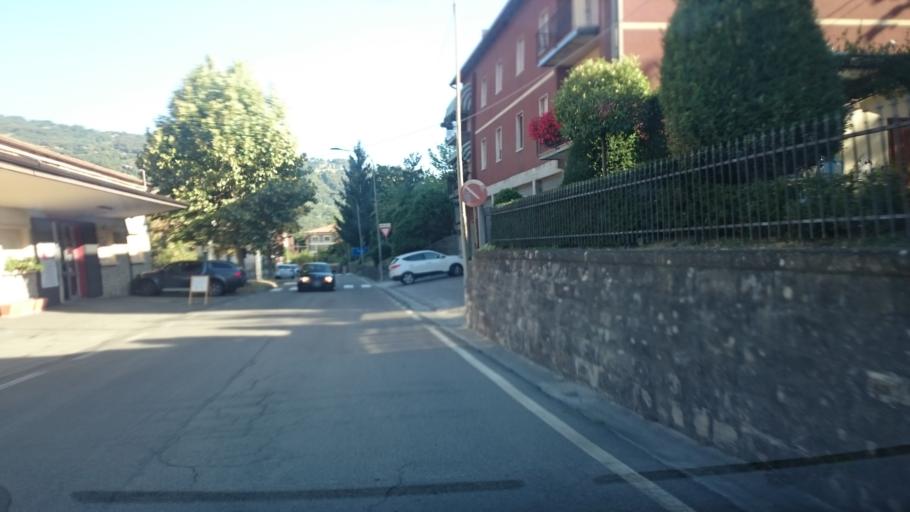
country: IT
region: Emilia-Romagna
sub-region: Provincia di Modena
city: Montefiorino
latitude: 44.4038
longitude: 10.6166
